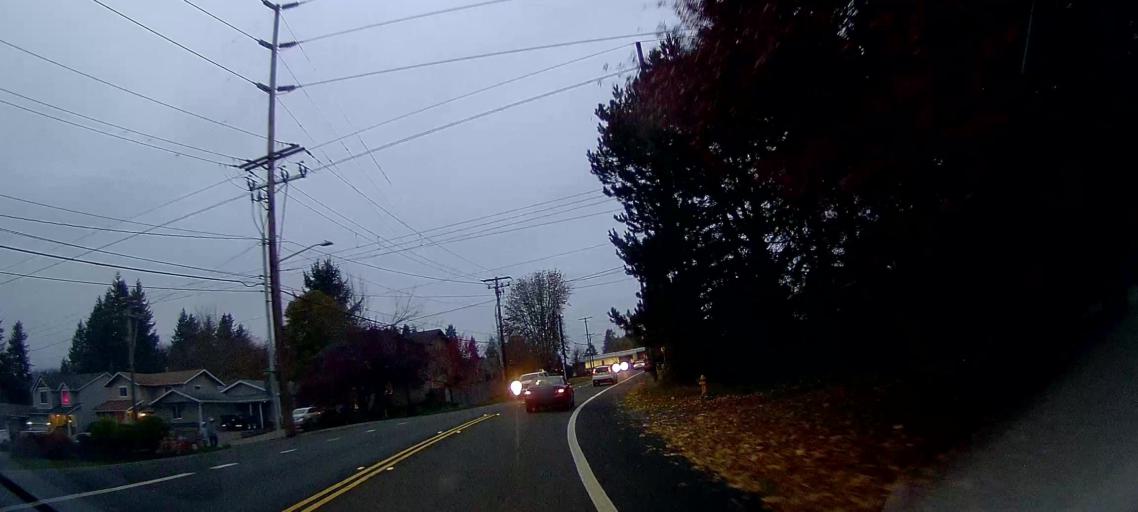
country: US
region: Washington
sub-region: Thurston County
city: Olympia
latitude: 47.0339
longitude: -122.8681
